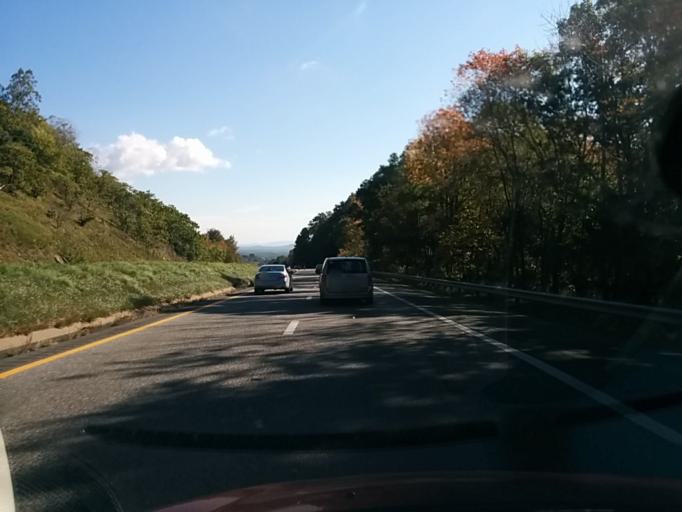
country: US
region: Virginia
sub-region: Augusta County
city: Dooms
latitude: 38.0431
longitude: -78.8020
